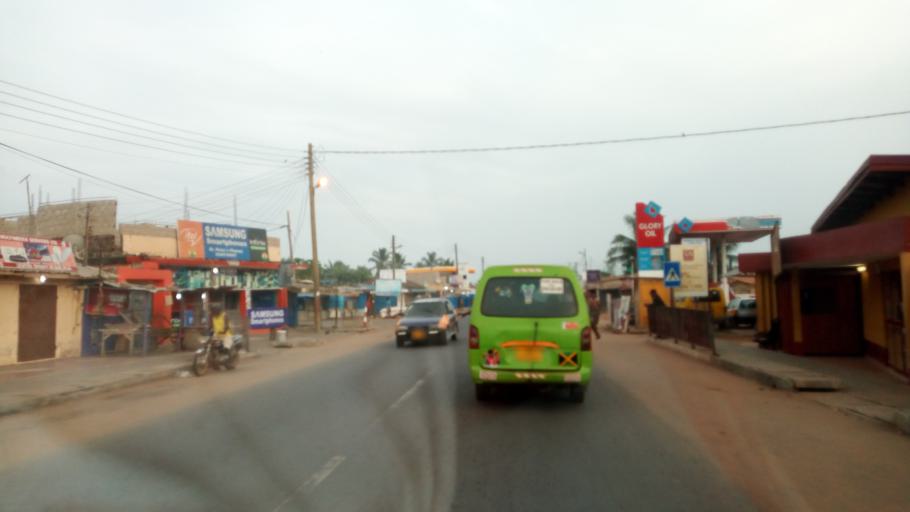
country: TG
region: Maritime
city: Lome
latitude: 6.1185
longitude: 1.1890
